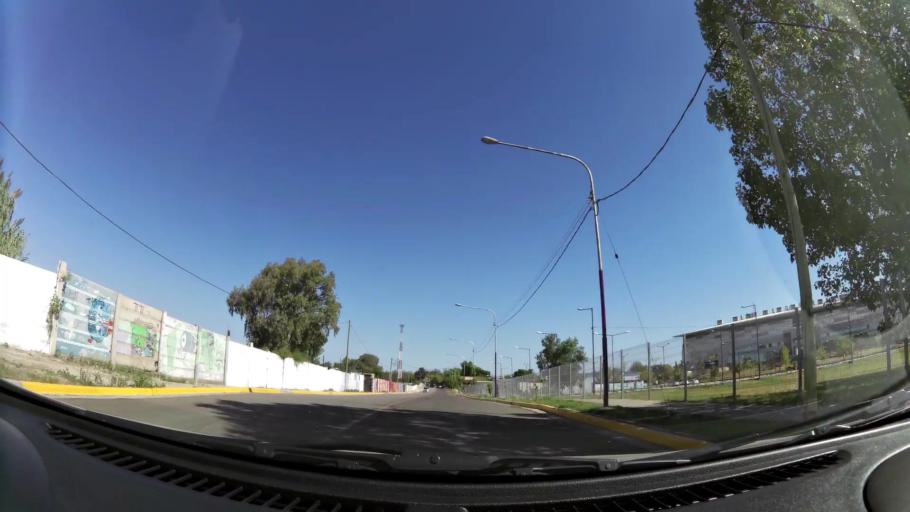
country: AR
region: Mendoza
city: Mendoza
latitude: -32.8870
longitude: -68.8126
